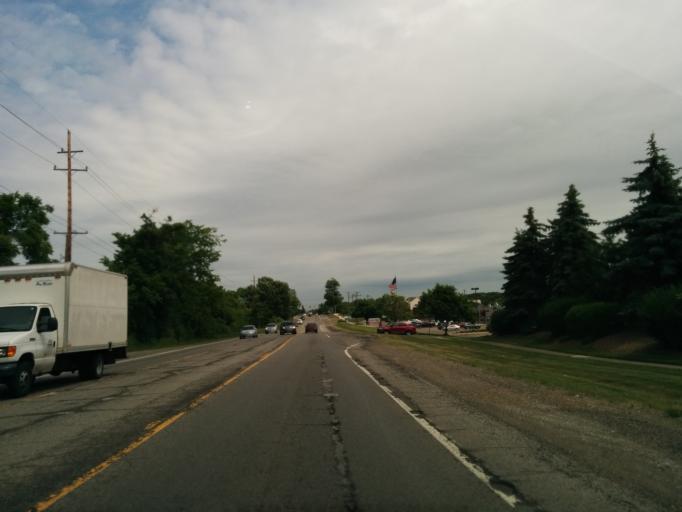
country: US
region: Michigan
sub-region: Oakland County
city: Walled Lake
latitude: 42.5229
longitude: -83.4375
